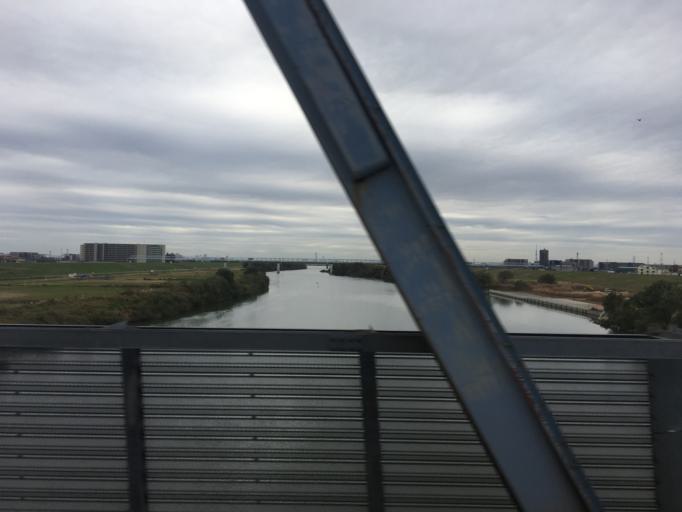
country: JP
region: Chiba
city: Nagareyama
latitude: 35.8446
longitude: 139.8900
